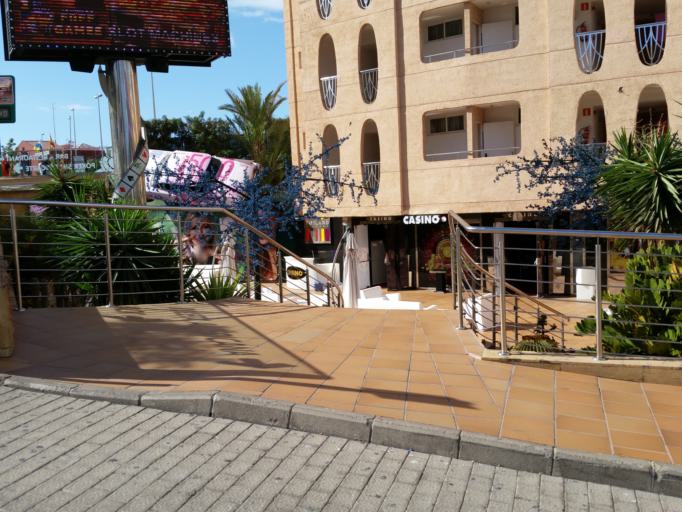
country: ES
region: Canary Islands
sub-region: Provincia de Las Palmas
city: Playa del Ingles
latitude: 27.7591
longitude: -15.5747
